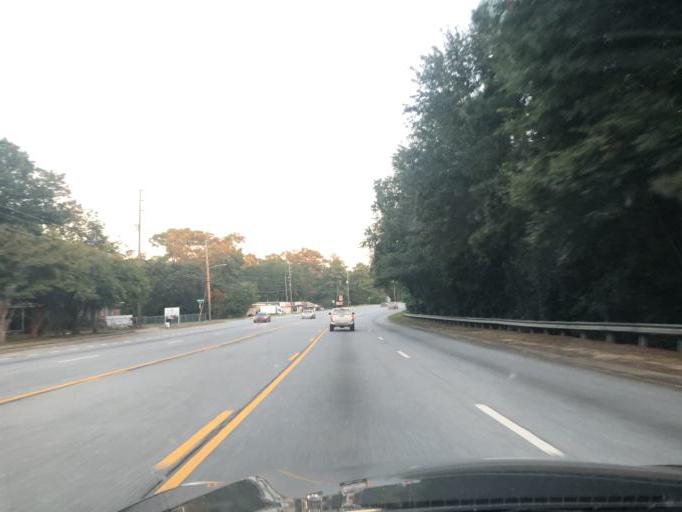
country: US
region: Georgia
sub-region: Muscogee County
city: Columbus
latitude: 32.4672
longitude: -84.9039
